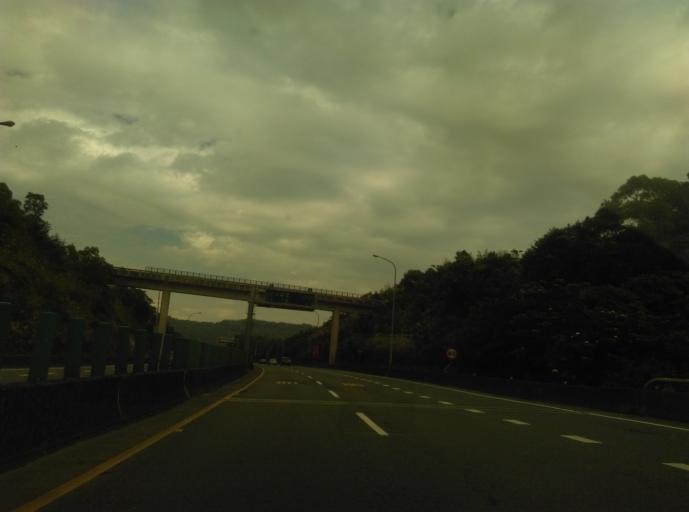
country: TW
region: Taiwan
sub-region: Keelung
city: Keelung
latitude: 25.1173
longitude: 121.6957
